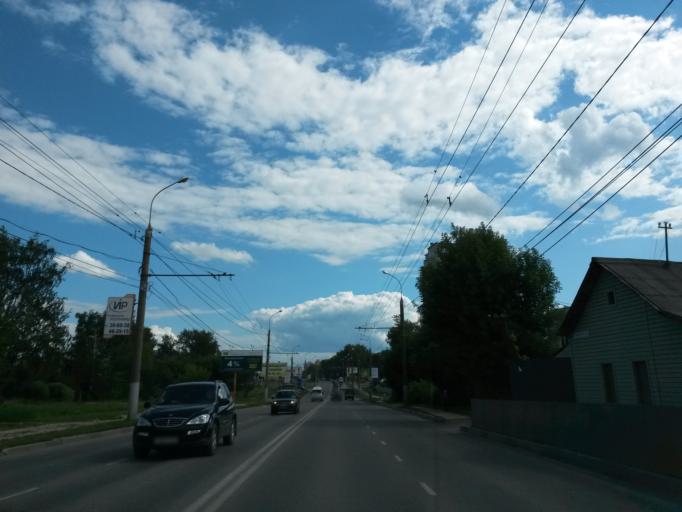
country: RU
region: Ivanovo
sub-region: Gorod Ivanovo
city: Ivanovo
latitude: 56.9771
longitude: 41.0054
